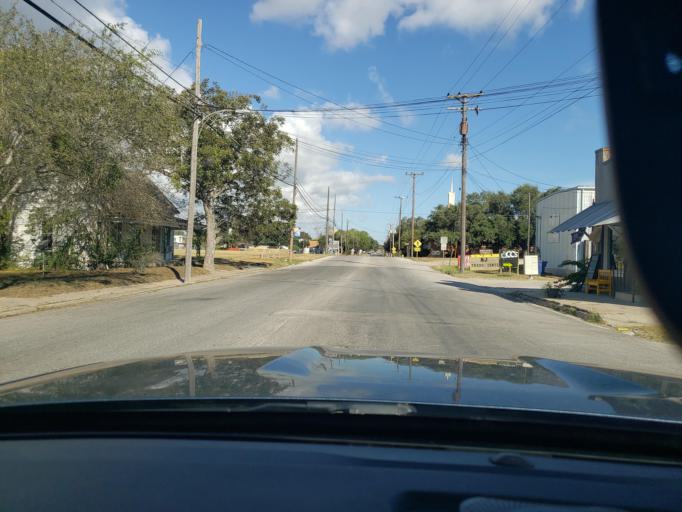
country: US
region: Texas
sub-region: Bee County
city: Beeville
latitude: 28.4057
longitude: -97.7502
